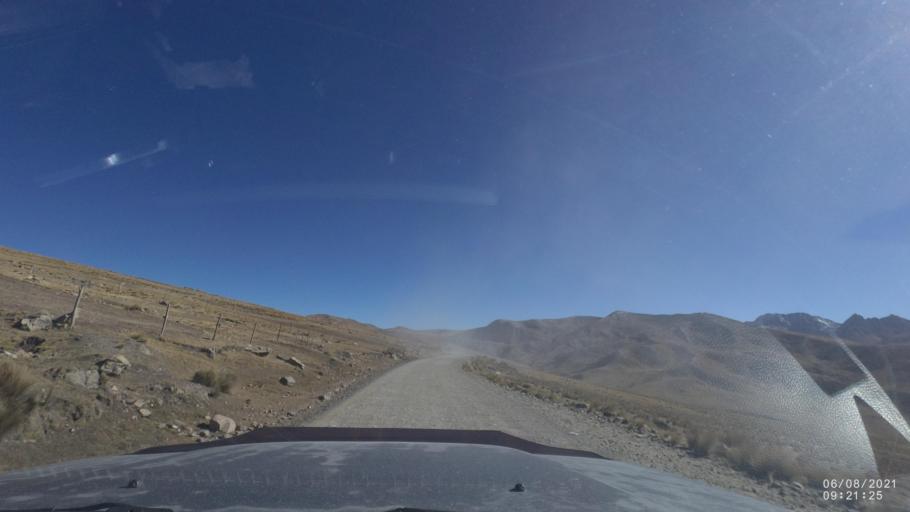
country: BO
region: Cochabamba
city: Colchani
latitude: -17.0210
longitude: -66.5441
